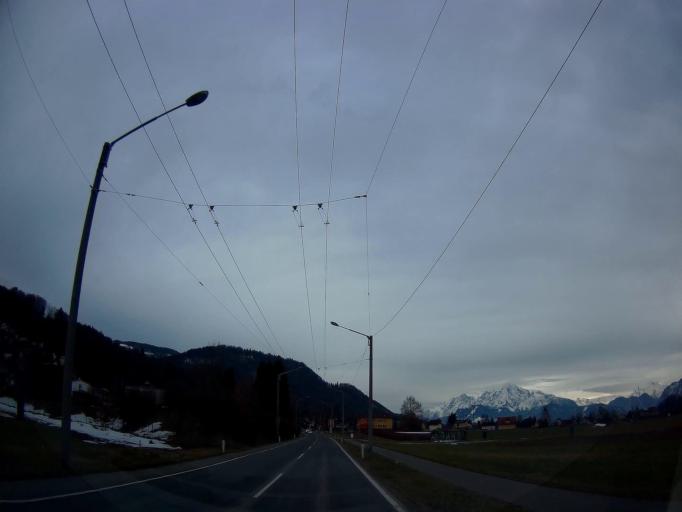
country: AT
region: Salzburg
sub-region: Politischer Bezirk Salzburg-Umgebung
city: Elsbethen
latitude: 47.7747
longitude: 13.0840
